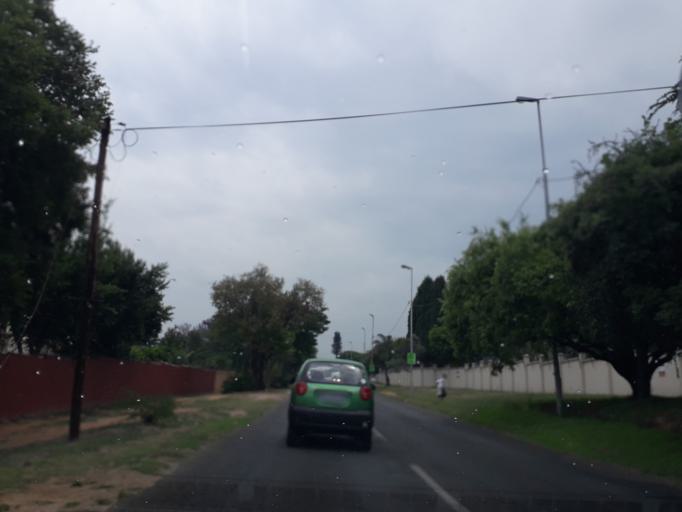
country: ZA
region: Gauteng
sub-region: City of Johannesburg Metropolitan Municipality
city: Roodepoort
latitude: -26.0798
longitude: 27.9476
